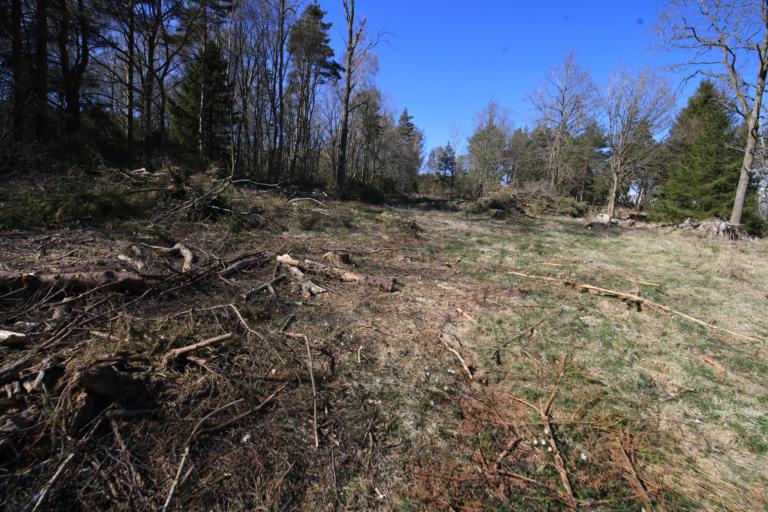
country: SE
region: Halland
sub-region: Varbergs Kommun
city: Varberg
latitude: 57.1684
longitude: 12.2704
